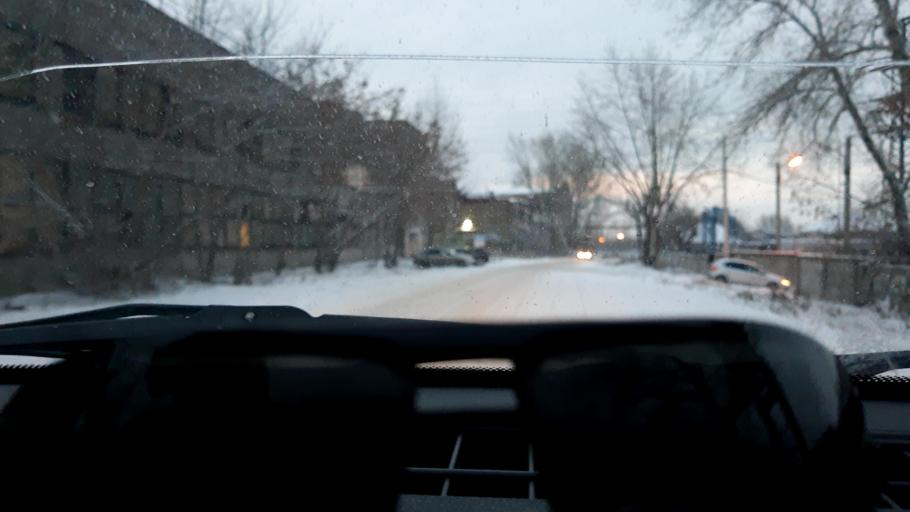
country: RU
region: Bashkortostan
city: Ufa
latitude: 54.8580
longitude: 56.0867
